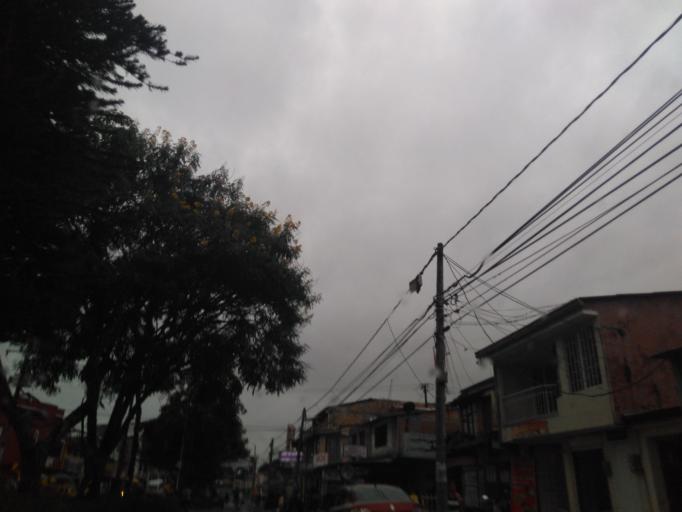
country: CO
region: Cauca
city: Popayan
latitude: 2.4462
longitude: -76.6116
